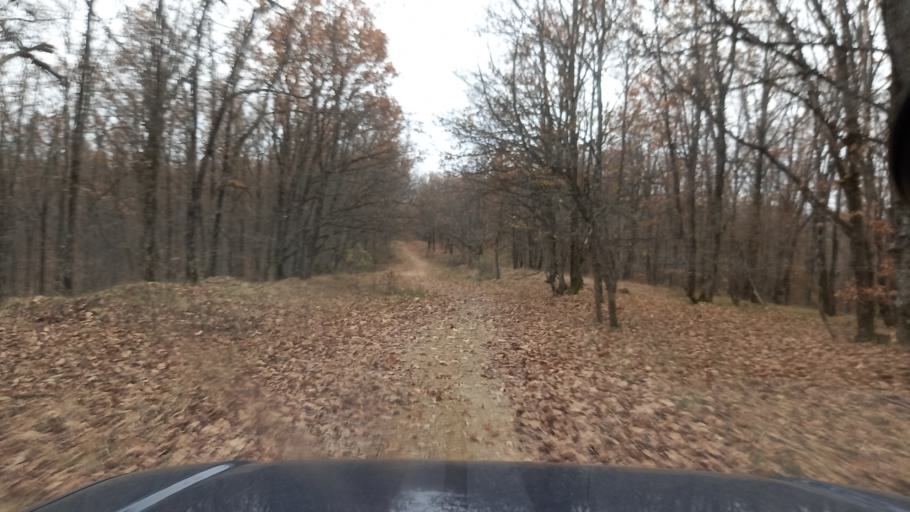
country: RU
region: Krasnodarskiy
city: Goryachiy Klyuch
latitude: 44.5035
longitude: 39.2836
